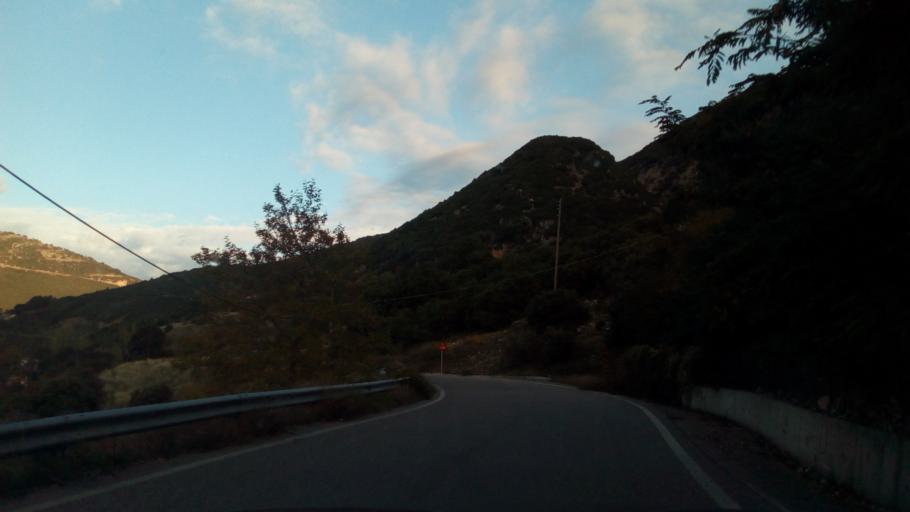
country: GR
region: West Greece
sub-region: Nomos Aitolias kai Akarnanias
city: Nafpaktos
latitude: 38.5274
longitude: 21.8334
